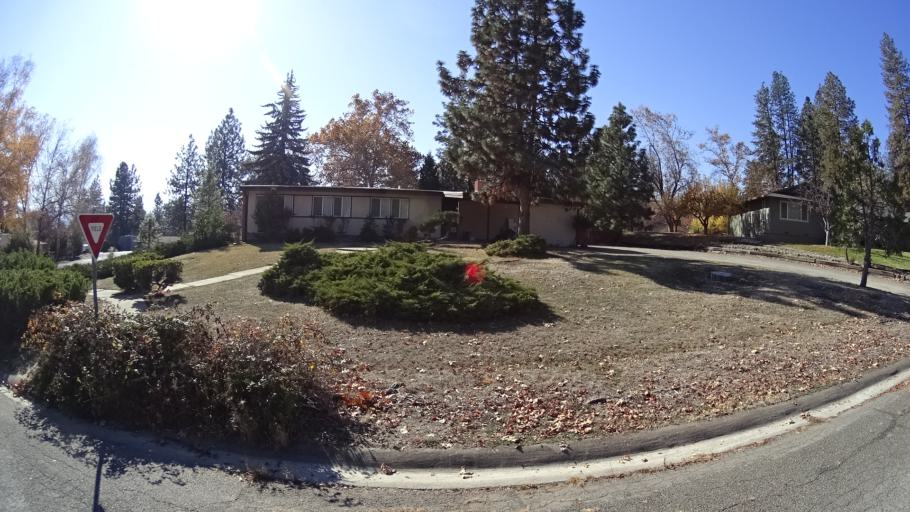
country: US
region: California
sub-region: Siskiyou County
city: Yreka
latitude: 41.7374
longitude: -122.6500
